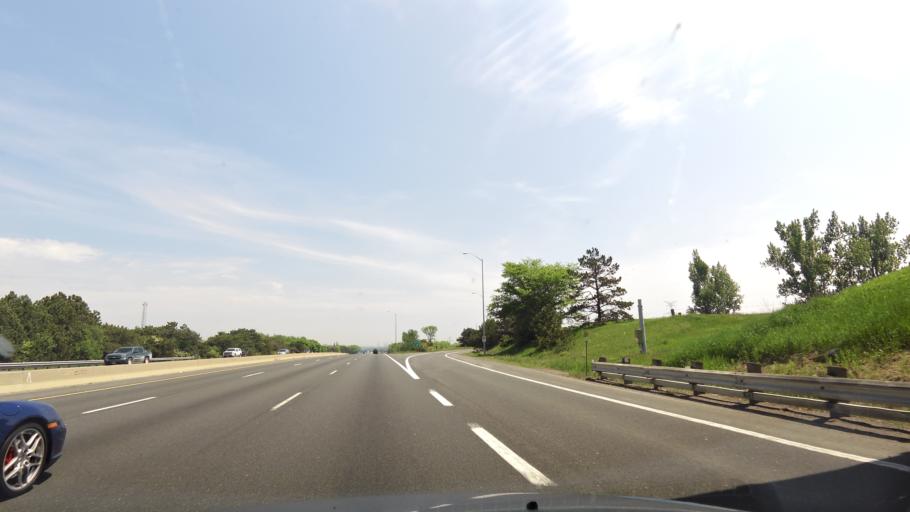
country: CA
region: Ontario
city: Oshawa
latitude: 43.9014
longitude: -78.6439
